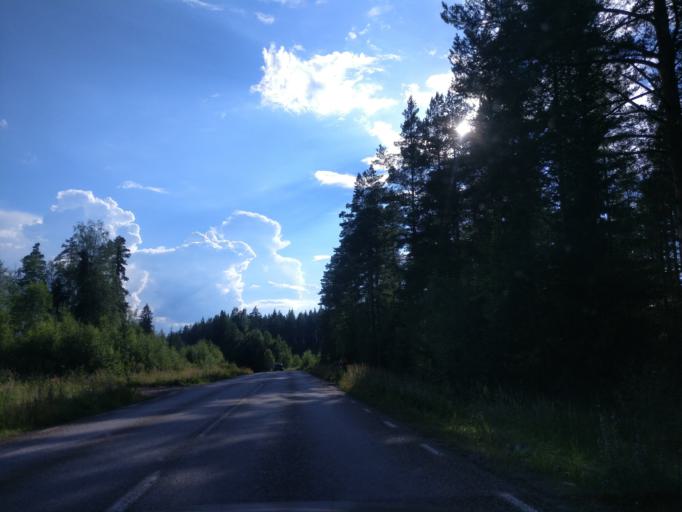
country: SE
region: Dalarna
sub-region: Ludvika Kommun
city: Ludvika
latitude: 60.2829
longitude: 15.0942
